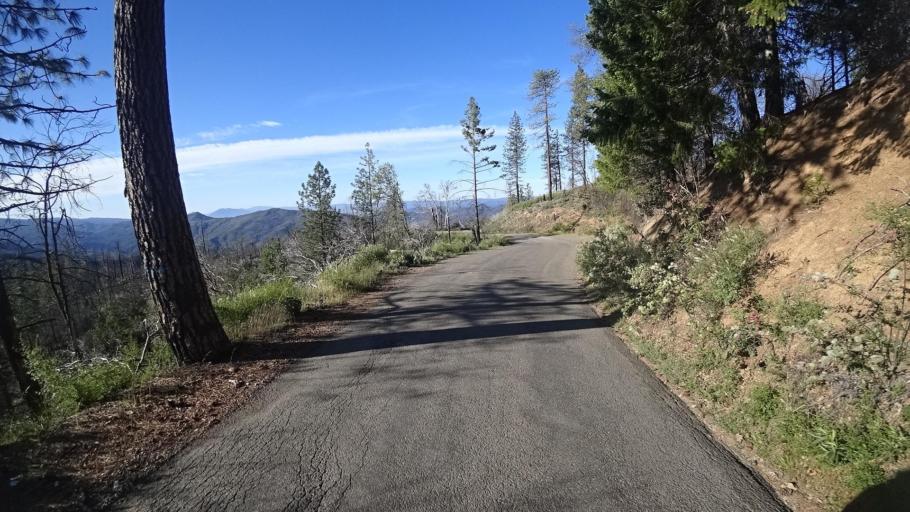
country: US
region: California
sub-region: Lake County
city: Upper Lake
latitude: 39.2844
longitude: -122.9265
